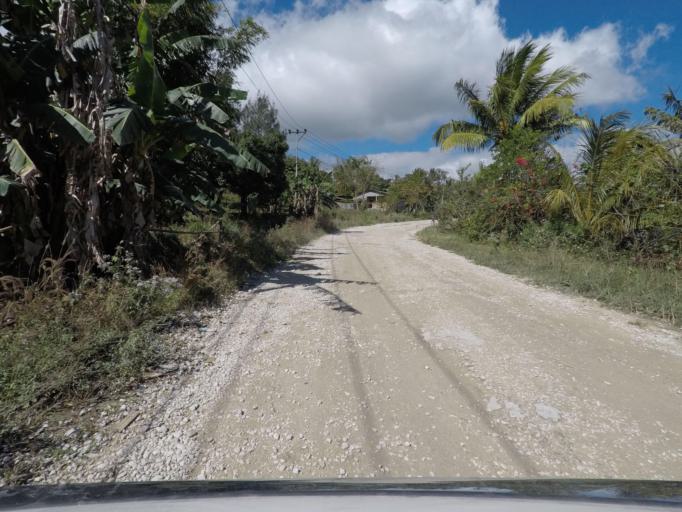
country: TL
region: Baucau
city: Venilale
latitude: -8.6719
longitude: 126.3665
